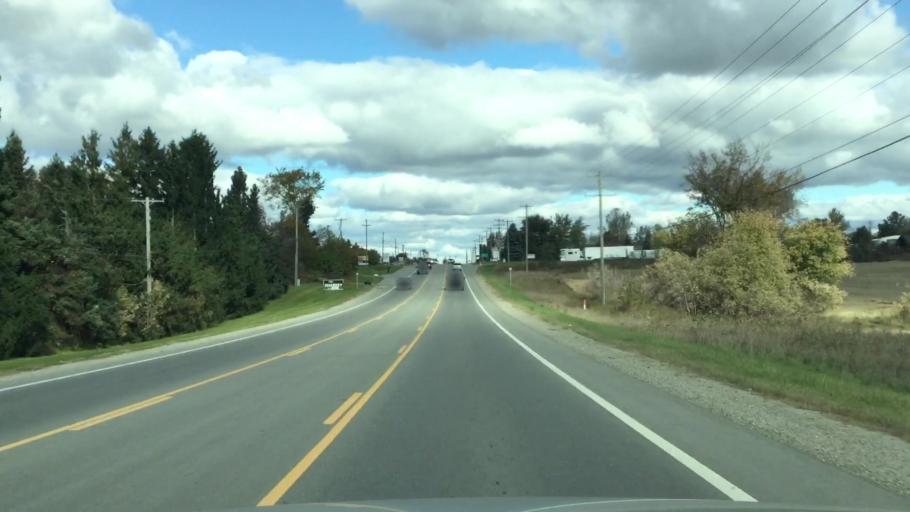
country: US
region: Michigan
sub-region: Lapeer County
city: Lapeer
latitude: 42.9515
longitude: -83.3137
